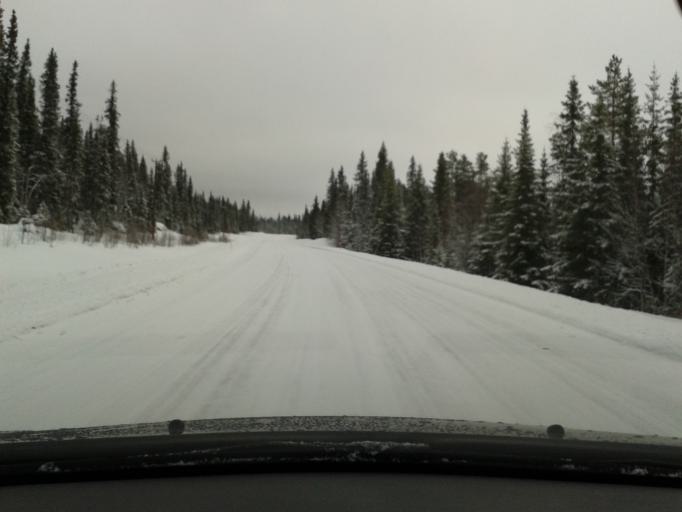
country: SE
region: Vaesterbotten
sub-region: Vilhelmina Kommun
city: Sjoberg
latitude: 65.2349
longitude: 15.8397
